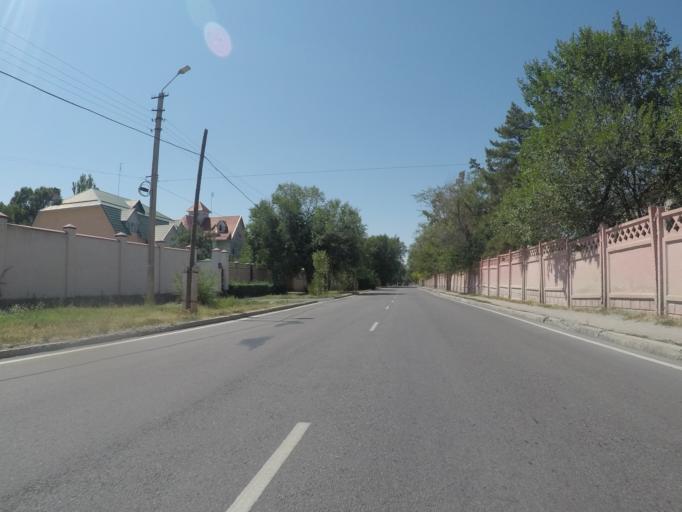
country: KG
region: Chuy
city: Bishkek
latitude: 42.8040
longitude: 74.5791
